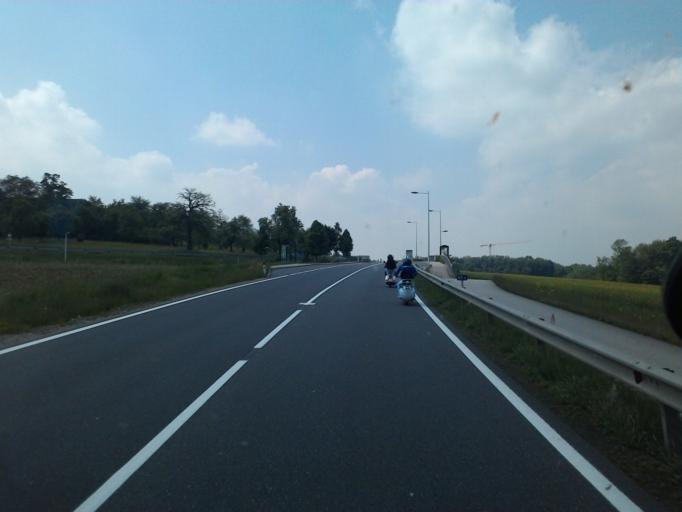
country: AT
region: Upper Austria
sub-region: Politischer Bezirk Steyr-Land
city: Bad Hall
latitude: 48.0268
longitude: 14.2367
